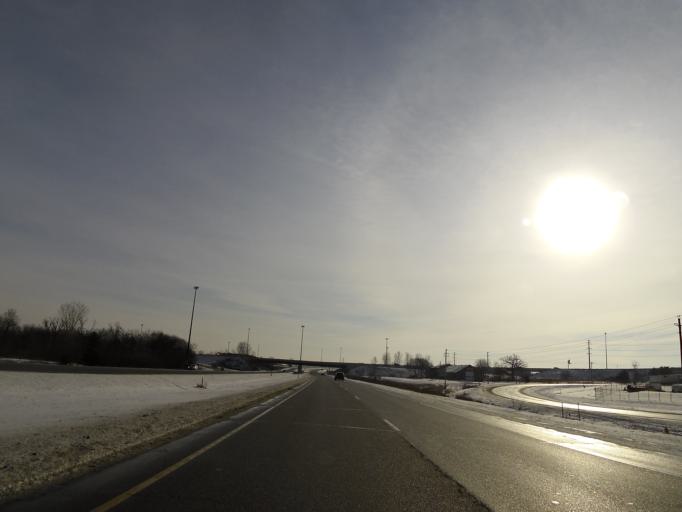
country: US
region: Minnesota
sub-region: Scott County
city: Savage
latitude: 44.7913
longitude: -93.4120
